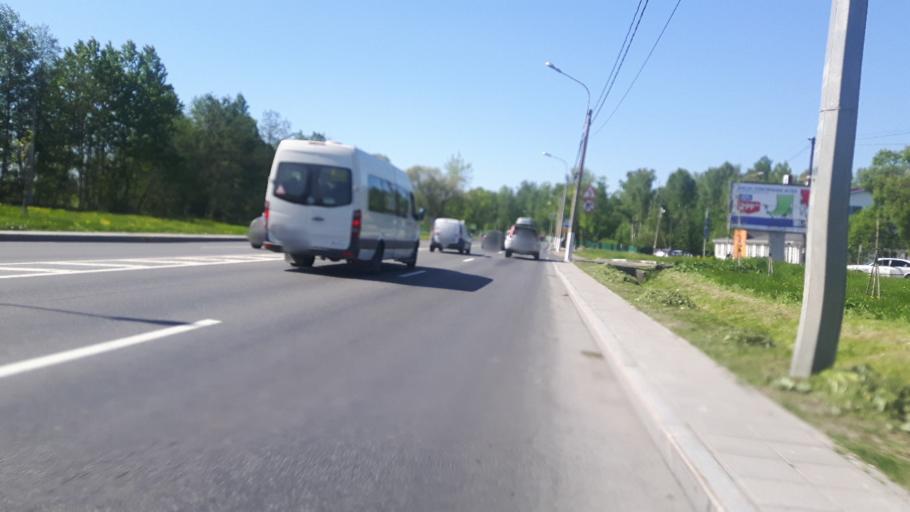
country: RU
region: Leningrad
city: Gorbunki
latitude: 59.8701
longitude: 29.9716
